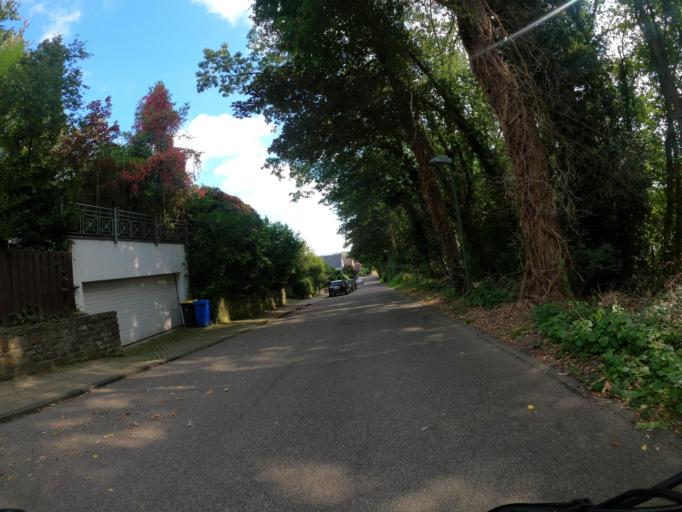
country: DE
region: North Rhine-Westphalia
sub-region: Regierungsbezirk Dusseldorf
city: Essen
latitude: 51.4112
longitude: 7.0634
